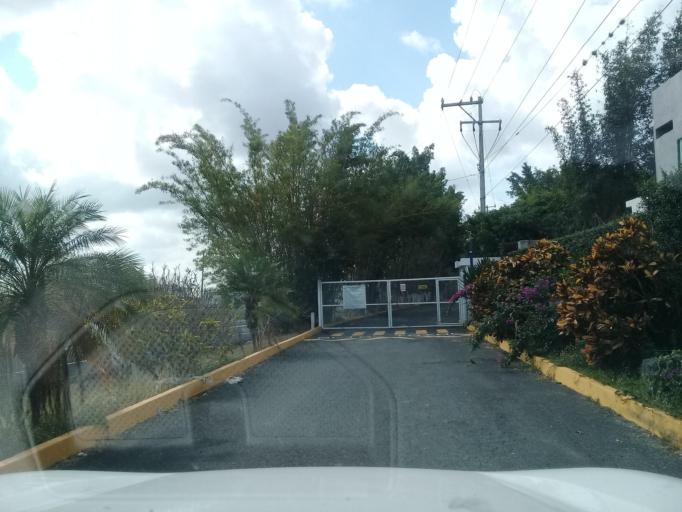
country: MX
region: Veracruz
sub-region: Emiliano Zapata
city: Plan del Rio
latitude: 19.4100
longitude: -96.6493
